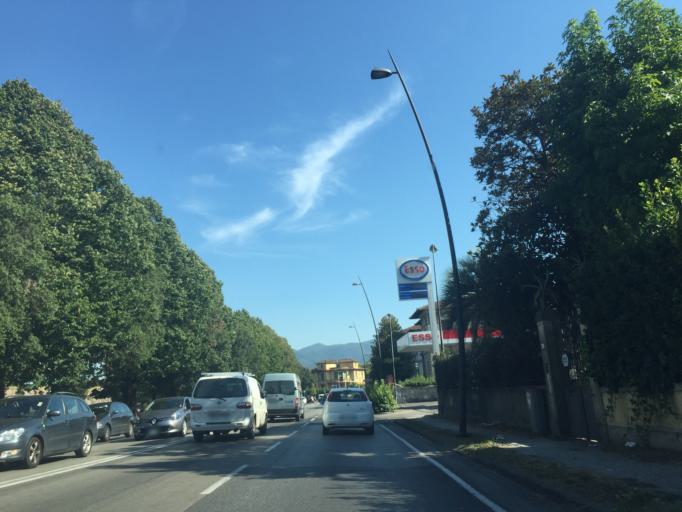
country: IT
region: Tuscany
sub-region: Provincia di Lucca
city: Lucca
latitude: 43.8411
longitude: 10.4947
